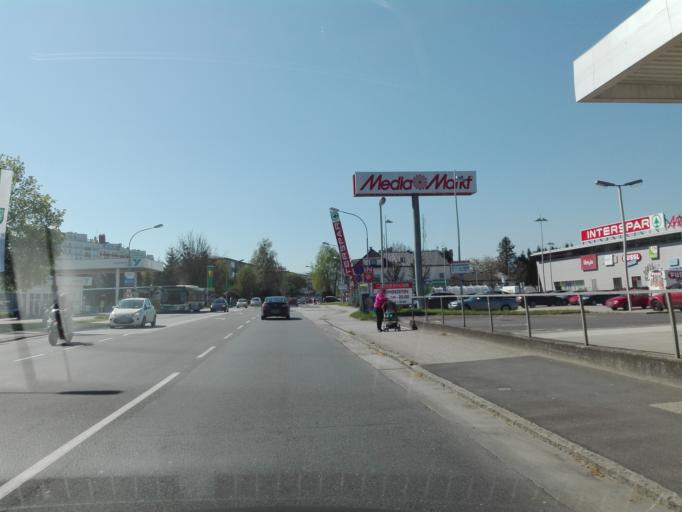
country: AT
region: Upper Austria
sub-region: Steyr Stadt
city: Steyr
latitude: 48.0537
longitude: 14.4205
